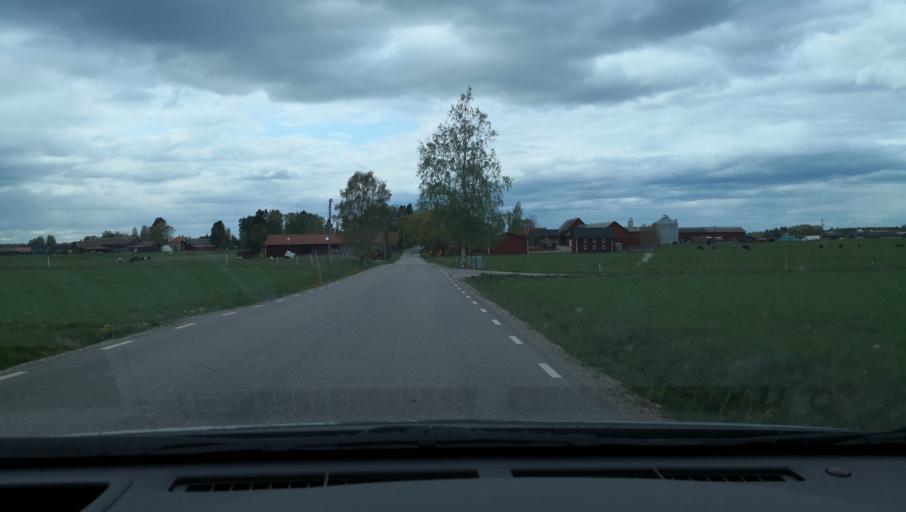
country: SE
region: Dalarna
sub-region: Avesta Kommun
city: Avesta
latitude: 60.0218
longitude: 16.3121
